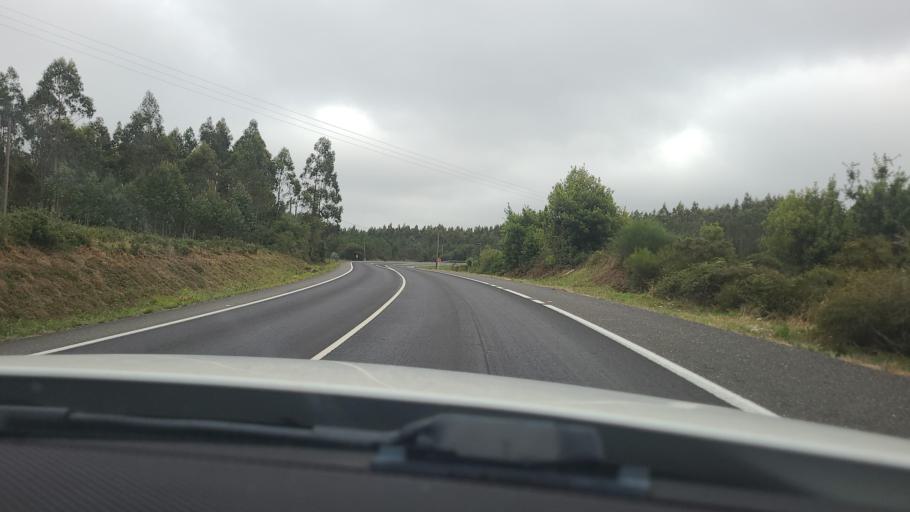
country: ES
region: Galicia
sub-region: Provincia da Coruna
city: Dumbria
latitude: 43.0115
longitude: -9.1477
